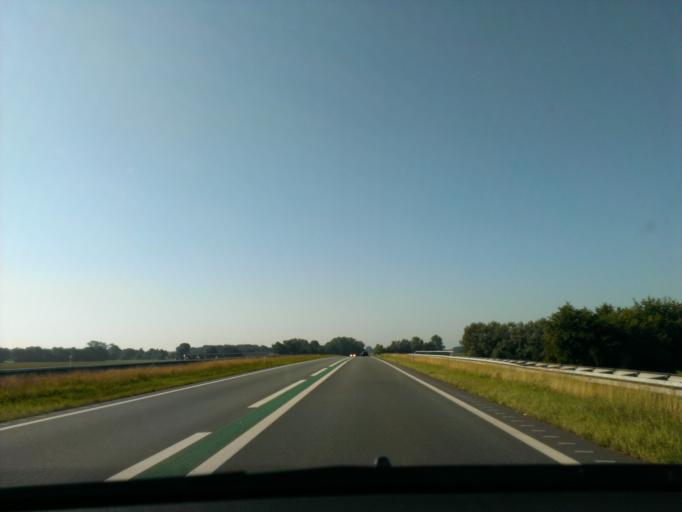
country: NL
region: Drenthe
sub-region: Gemeente Coevorden
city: Dalen
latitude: 52.6975
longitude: 6.7440
